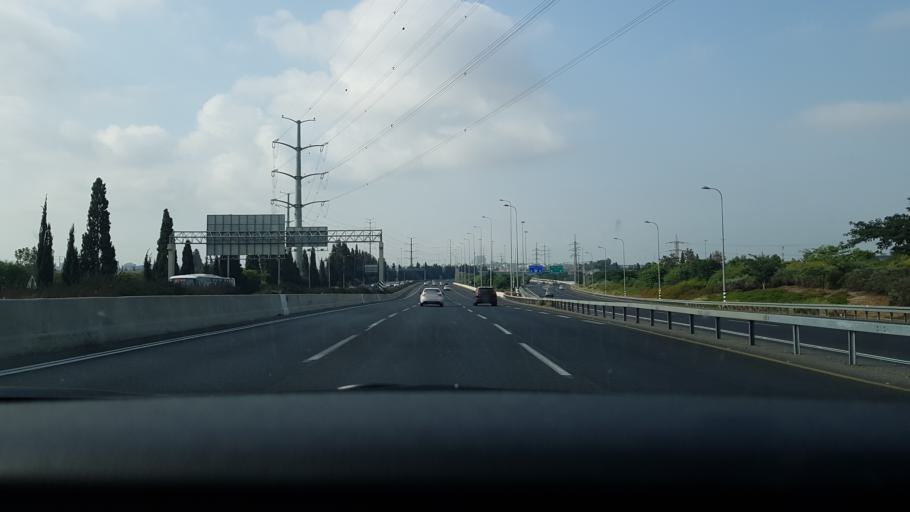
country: IL
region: Central District
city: Bet Dagan
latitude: 32.0066
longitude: 34.8120
